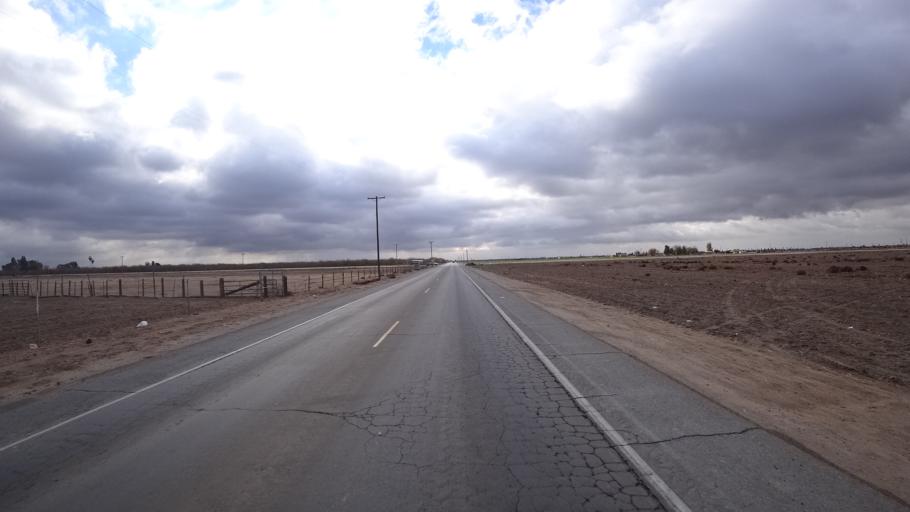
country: US
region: California
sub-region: Kern County
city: Greenfield
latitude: 35.2937
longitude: -118.9855
